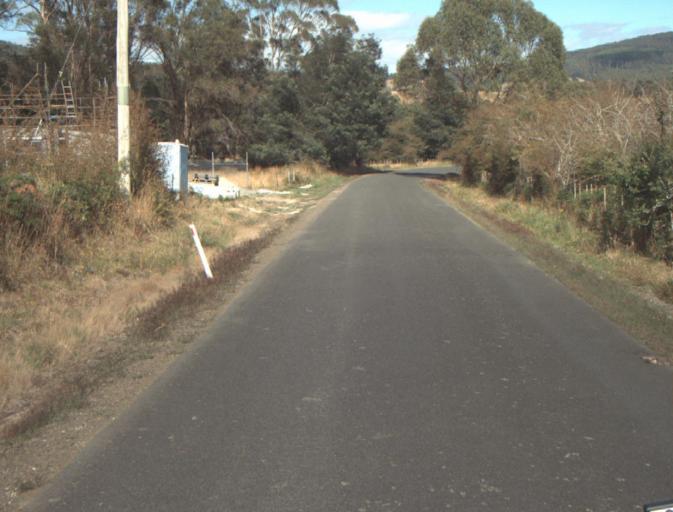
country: AU
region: Tasmania
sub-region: Launceston
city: Mayfield
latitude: -41.2600
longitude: 147.1670
